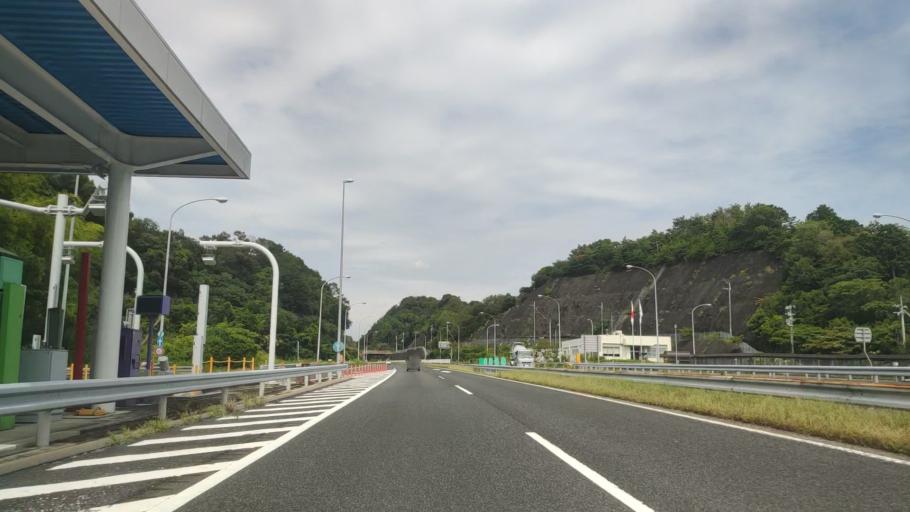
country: JP
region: Wakayama
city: Kainan
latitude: 34.1580
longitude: 135.2318
